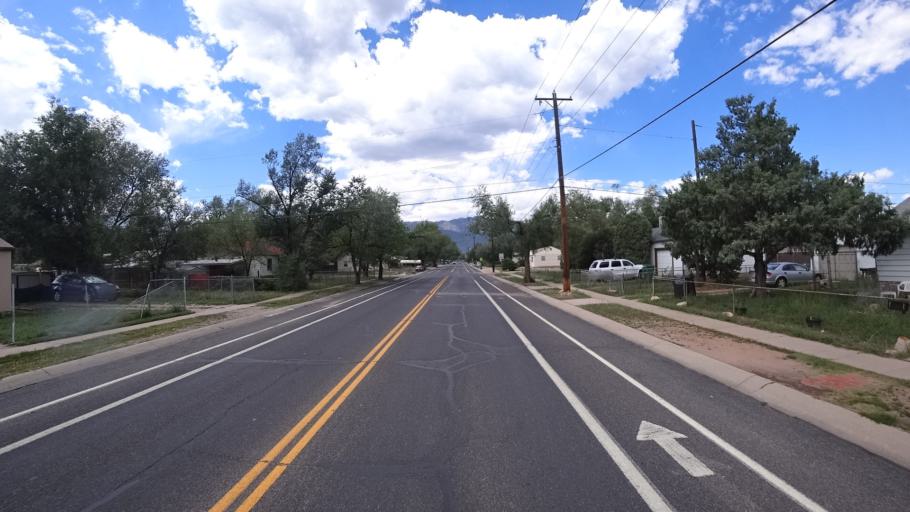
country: US
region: Colorado
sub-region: El Paso County
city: Colorado Springs
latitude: 38.8069
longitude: -104.8155
